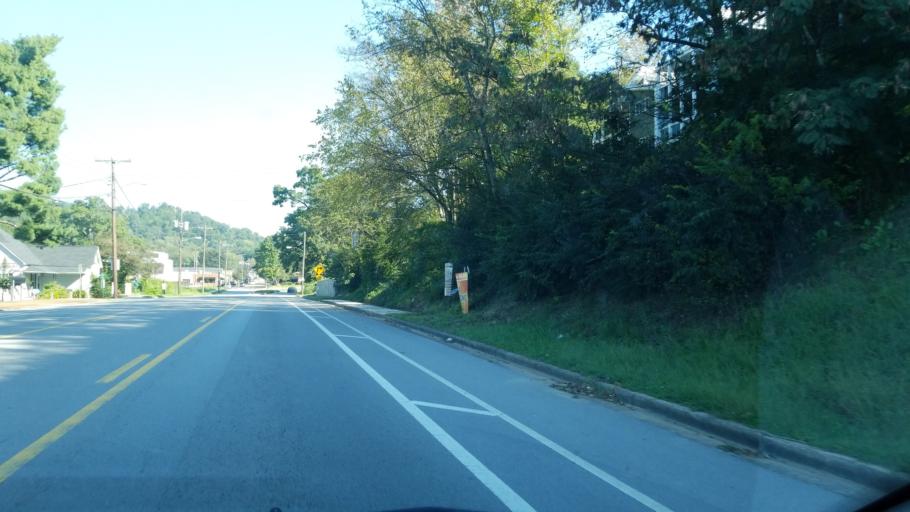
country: US
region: Tennessee
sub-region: Hamilton County
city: Chattanooga
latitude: 35.0695
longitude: -85.3088
